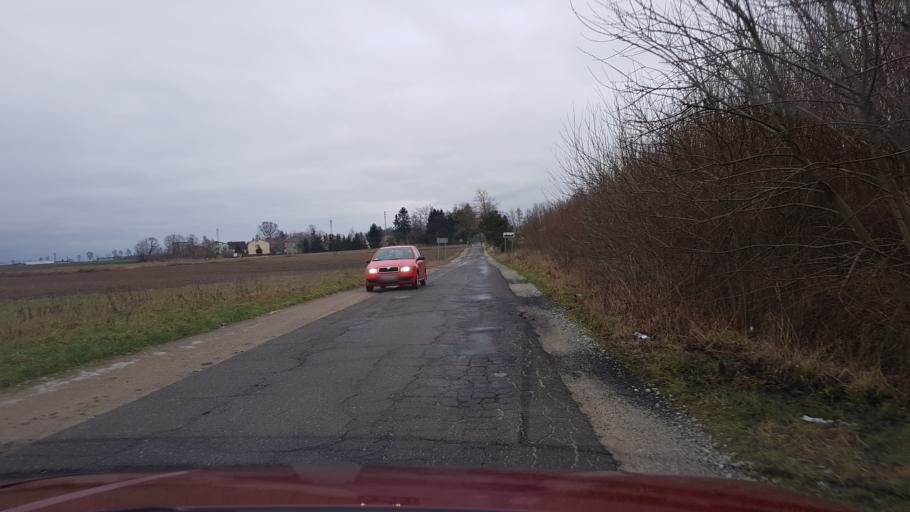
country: PL
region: West Pomeranian Voivodeship
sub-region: Powiat koszalinski
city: Mielno
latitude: 54.1411
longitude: 16.0342
